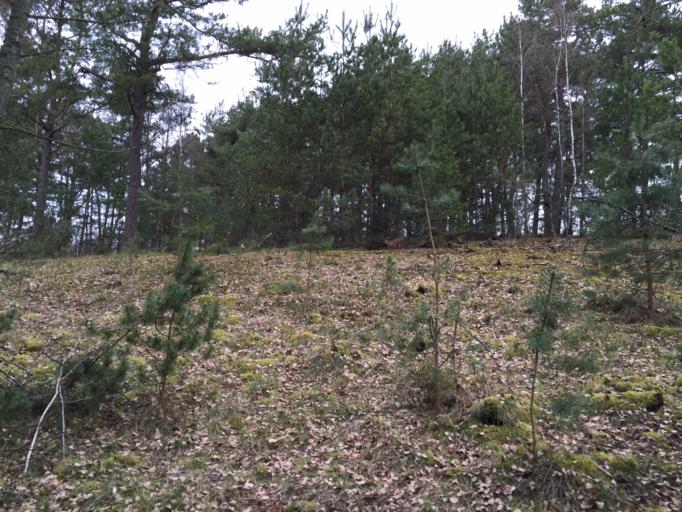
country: LT
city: Nida
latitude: 55.3048
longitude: 20.9969
